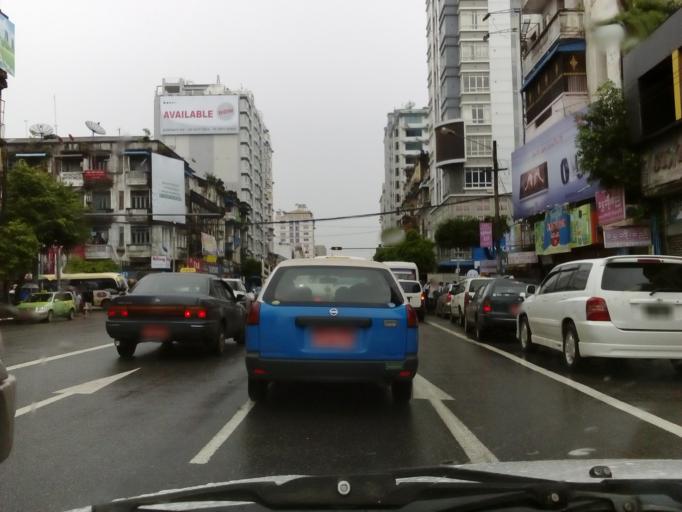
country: MM
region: Yangon
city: Yangon
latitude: 16.7773
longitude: 96.1617
